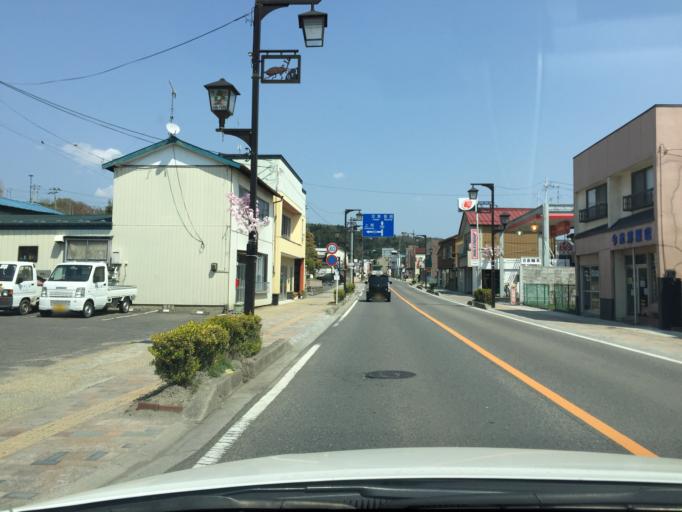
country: JP
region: Fukushima
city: Funehikimachi-funehiki
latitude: 37.4387
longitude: 140.6409
